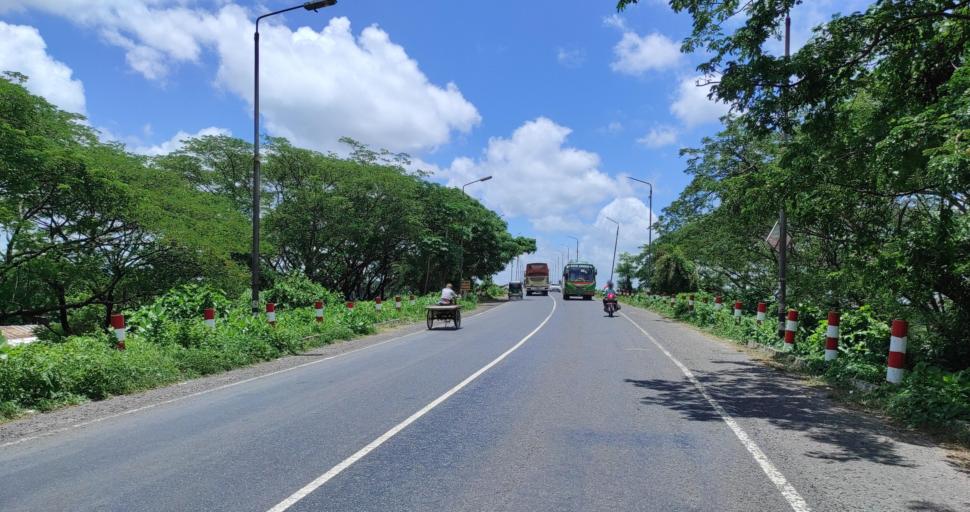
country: BD
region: Barisal
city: Gaurnadi
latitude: 22.8257
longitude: 90.2612
